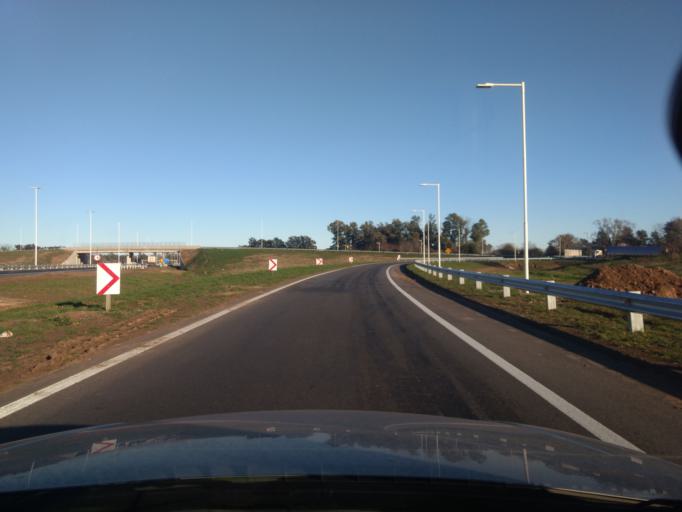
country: AR
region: Buenos Aires
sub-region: Partido de Lujan
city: Lujan
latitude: -34.5894
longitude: -59.1019
